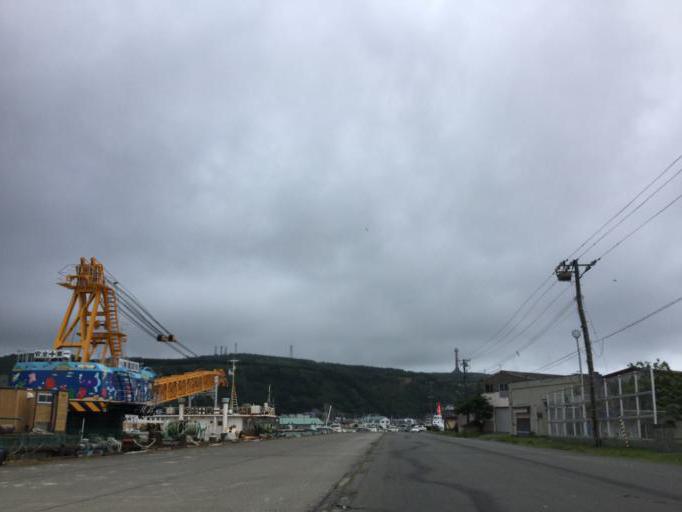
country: JP
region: Hokkaido
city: Wakkanai
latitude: 45.4044
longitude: 141.6821
